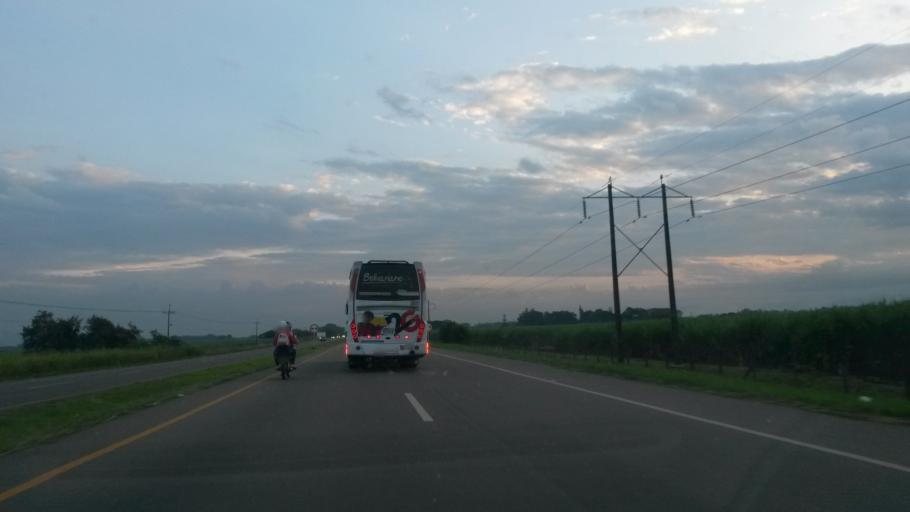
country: CO
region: Cauca
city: Caloto
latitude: 3.0998
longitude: -76.4691
